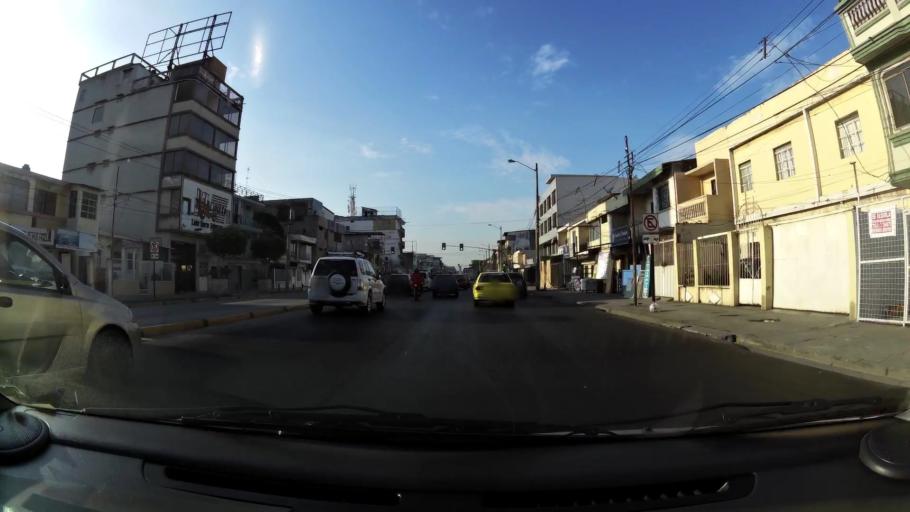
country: EC
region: Guayas
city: Guayaquil
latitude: -2.2177
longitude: -79.8980
